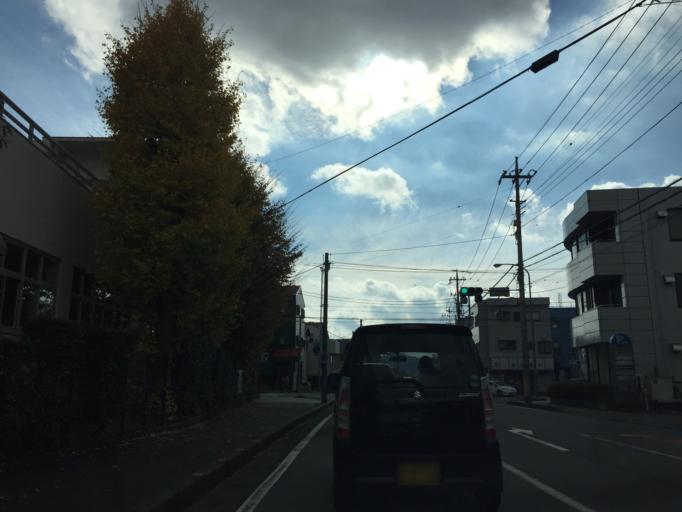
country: JP
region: Shizuoka
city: Mishima
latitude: 35.1324
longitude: 138.8985
